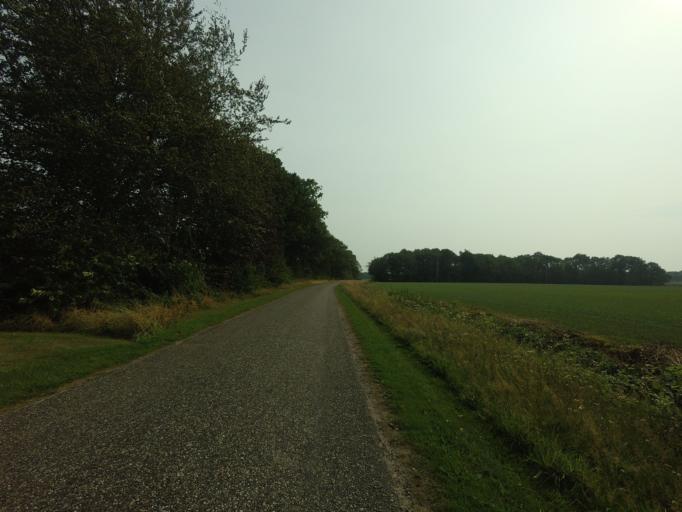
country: NL
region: Drenthe
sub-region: Gemeente Tynaarlo
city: Vries
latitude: 53.1132
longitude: 6.5422
